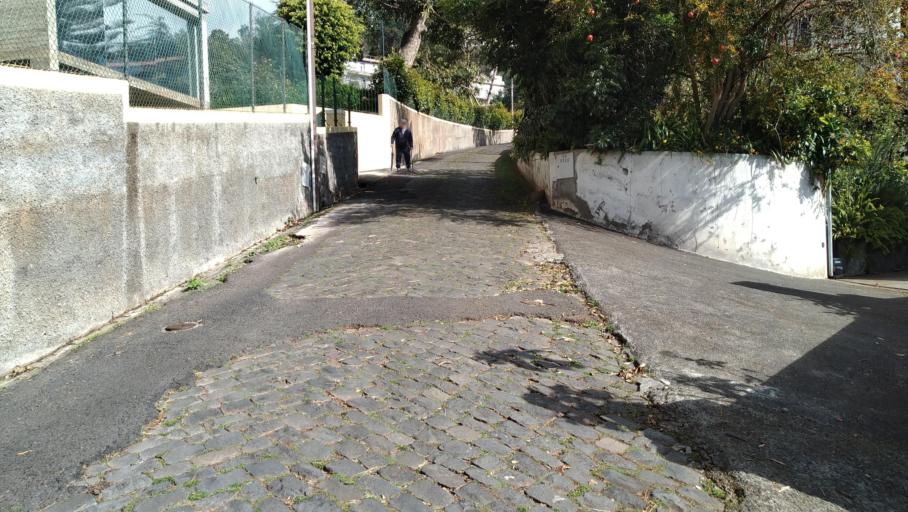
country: PT
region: Madeira
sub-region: Funchal
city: Nossa Senhora do Monte
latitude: 32.6591
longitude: -16.8784
